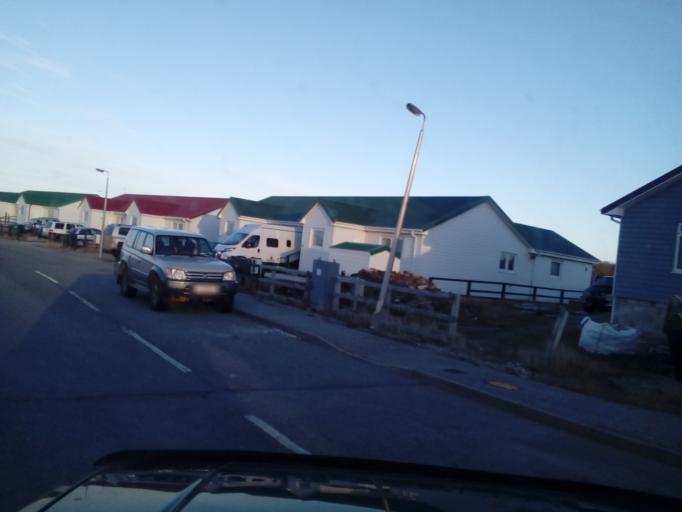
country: FK
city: Stanley
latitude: -51.6966
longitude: -57.8383
